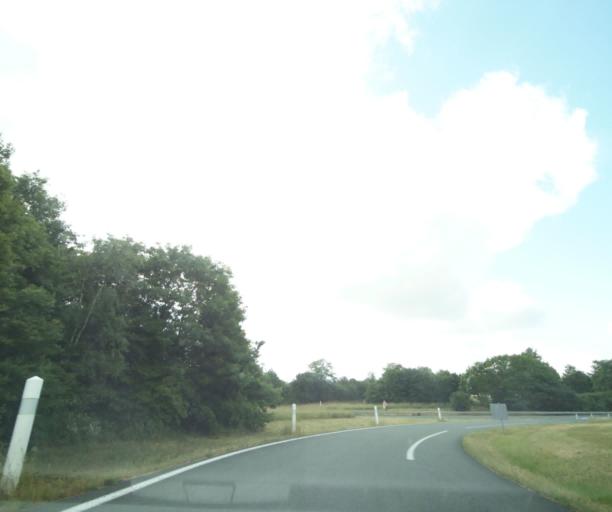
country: FR
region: Pays de la Loire
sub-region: Departement de la Sarthe
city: Vion
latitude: 47.7799
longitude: -0.2055
